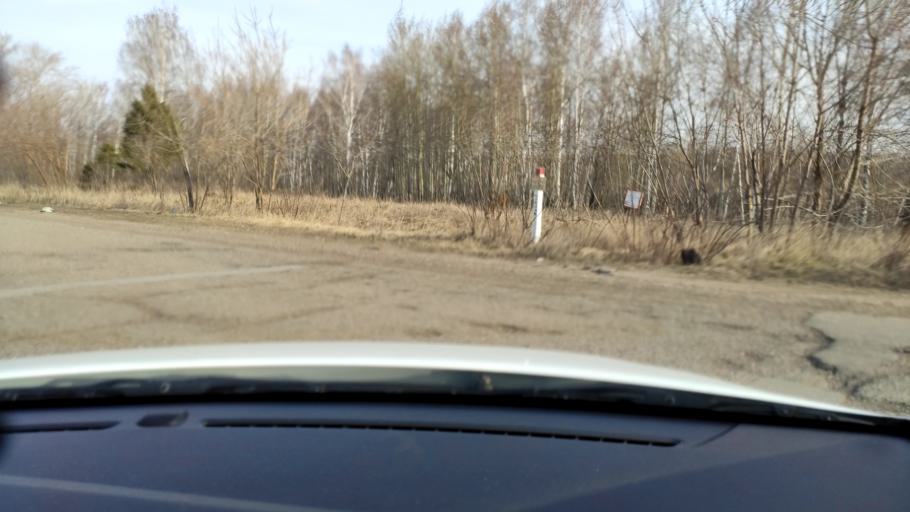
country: RU
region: Tatarstan
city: Stolbishchi
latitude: 55.7173
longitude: 49.2187
